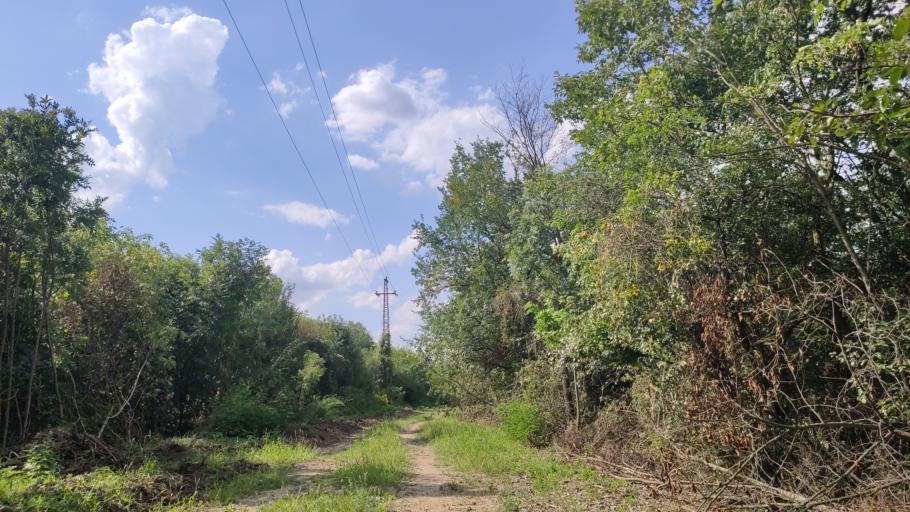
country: HU
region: Pest
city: Biatorbagy
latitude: 47.4637
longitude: 18.8697
